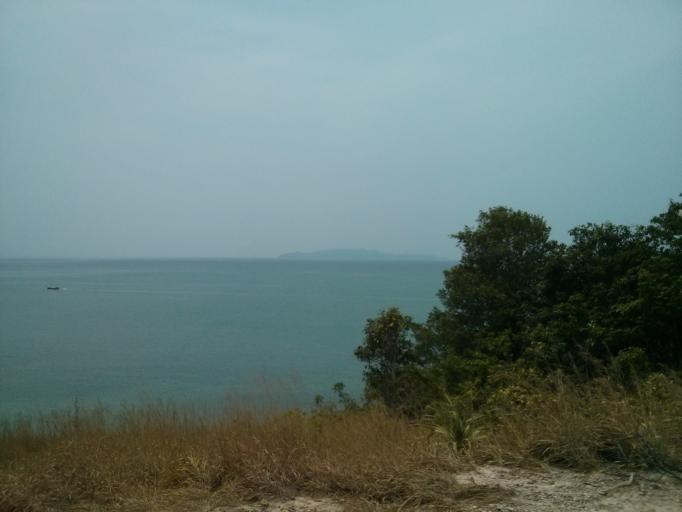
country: TH
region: Krabi
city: Ko Lanta
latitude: 7.4686
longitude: 99.0980
